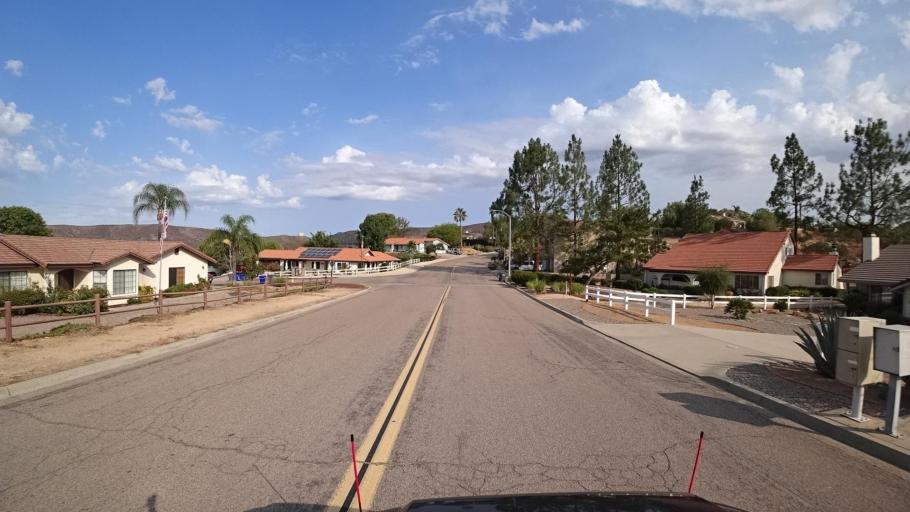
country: US
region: California
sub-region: San Diego County
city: San Diego Country Estates
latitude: 33.0129
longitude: -116.7999
